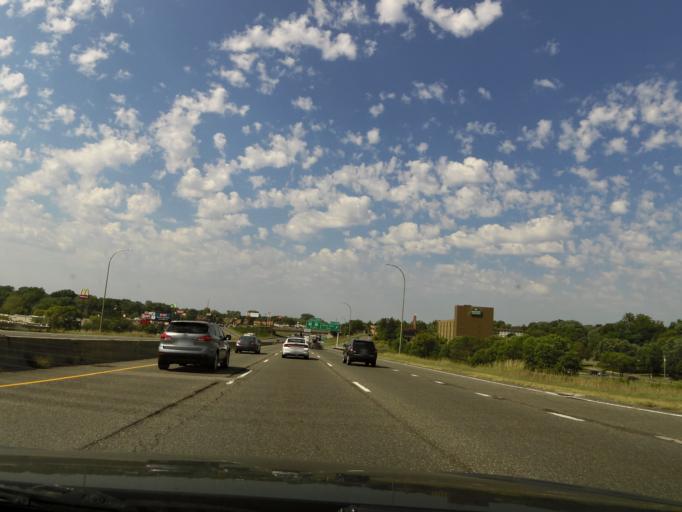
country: US
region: Minnesota
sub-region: Ramsey County
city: Maplewood
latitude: 44.9515
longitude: -93.0198
